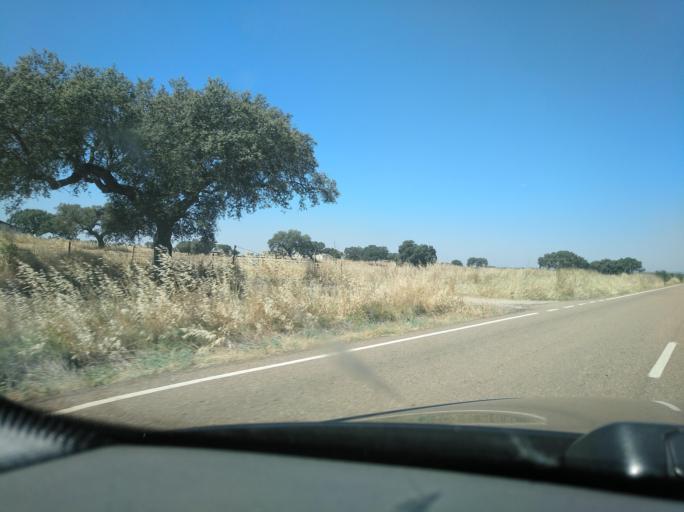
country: ES
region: Extremadura
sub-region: Provincia de Badajoz
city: Olivenza
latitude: 38.7020
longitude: -7.1582
